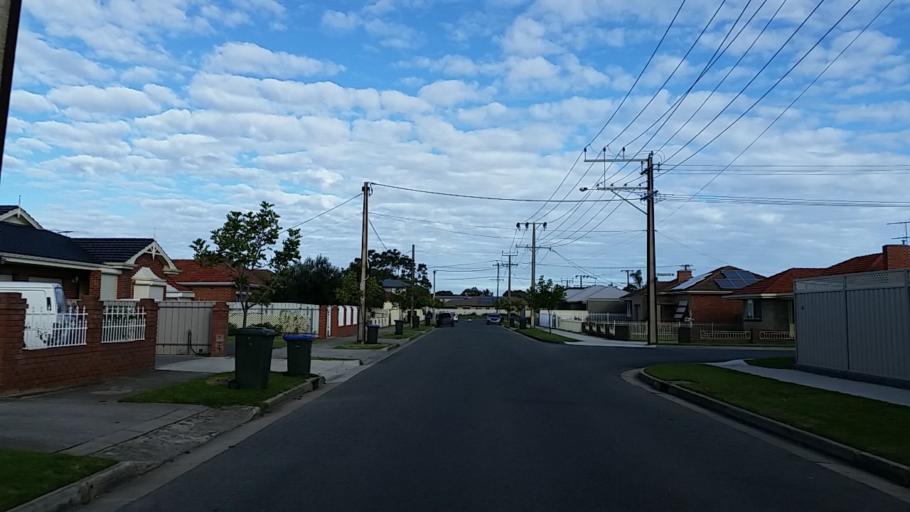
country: AU
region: South Australia
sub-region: Charles Sturt
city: Seaton
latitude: -34.8921
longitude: 138.5190
